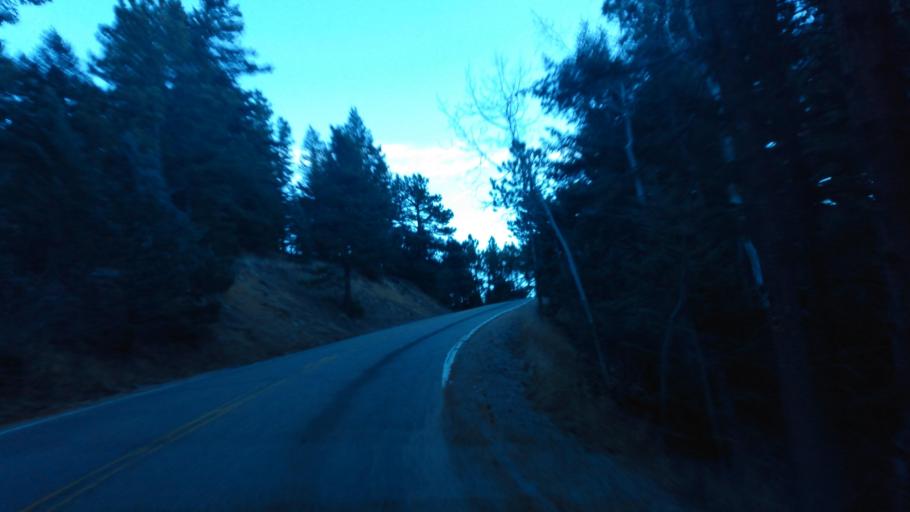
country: US
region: Colorado
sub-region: Boulder County
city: Coal Creek
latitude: 39.9852
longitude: -105.3775
